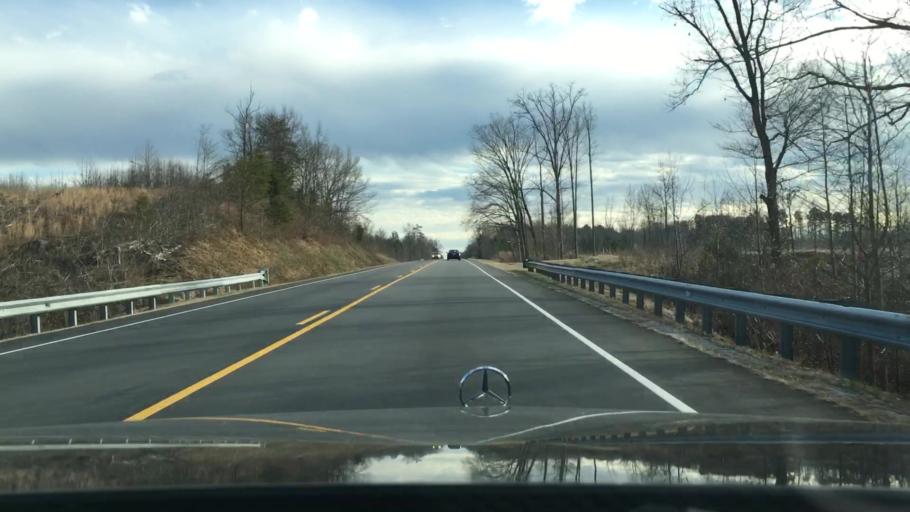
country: US
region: Virginia
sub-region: City of Danville
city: Danville
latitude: 36.5021
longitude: -79.3880
